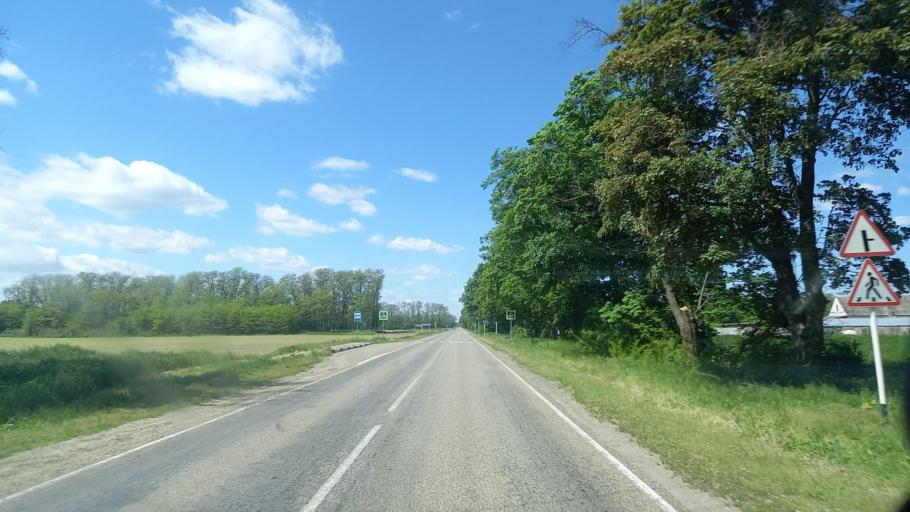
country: RU
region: Krasnodarskiy
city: Kazanskaya
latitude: 45.3679
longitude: 40.4182
